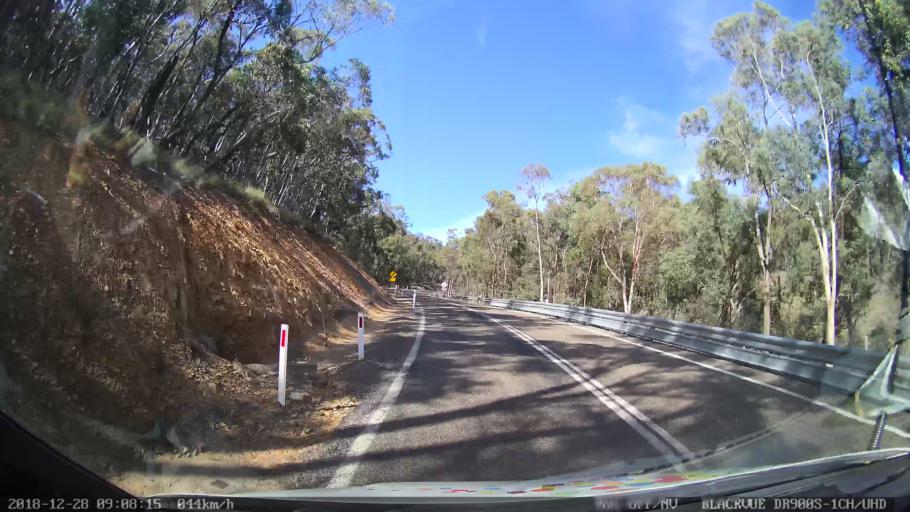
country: AU
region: New South Wales
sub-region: Upper Lachlan Shire
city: Crookwell
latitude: -34.2120
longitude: 149.3404
